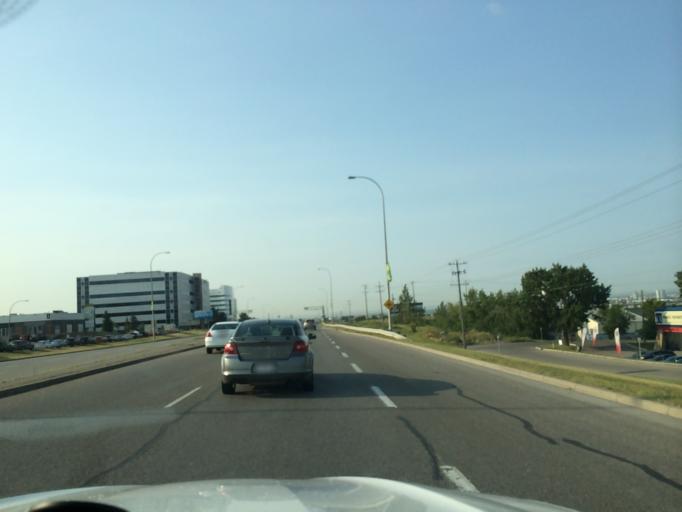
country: CA
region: Alberta
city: Calgary
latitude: 51.0520
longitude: -114.0019
